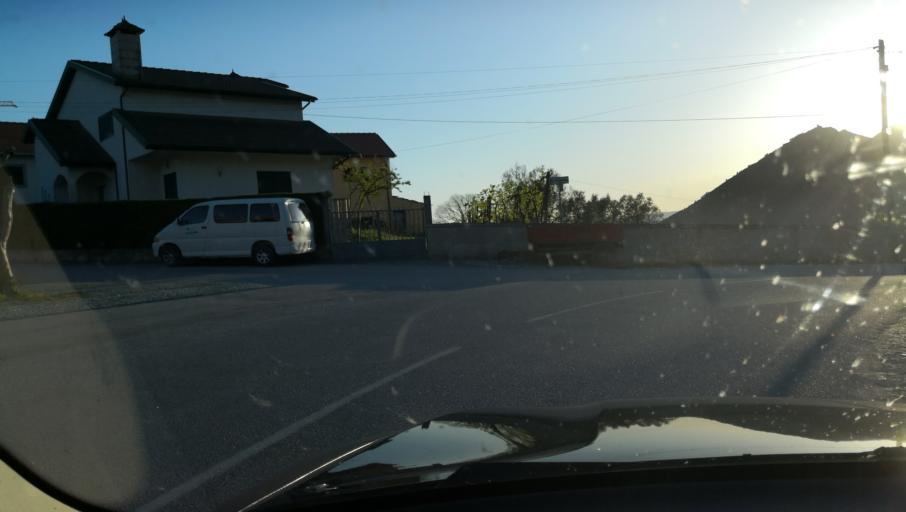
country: PT
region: Vila Real
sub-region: Mondim de Basto
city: Mondim de Basto
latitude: 41.4116
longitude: -7.8776
